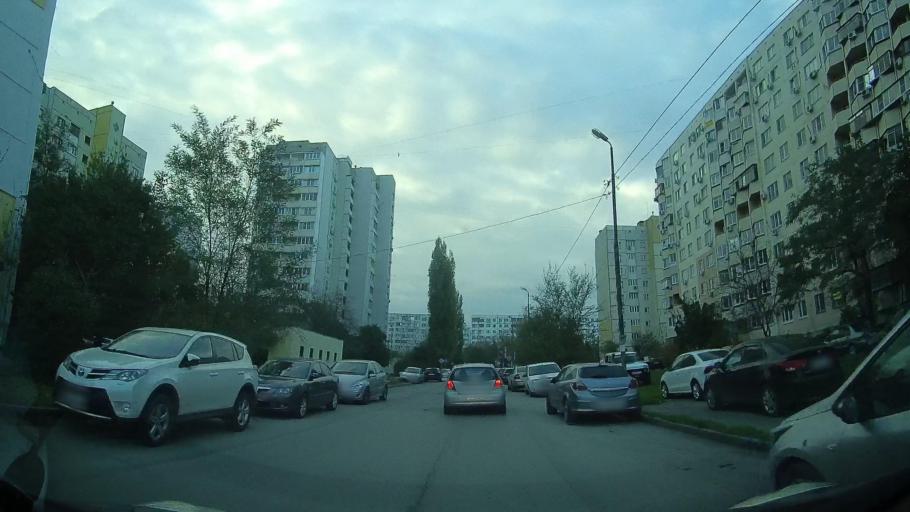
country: RU
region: Rostov
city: Severnyy
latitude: 47.2591
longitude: 39.6439
